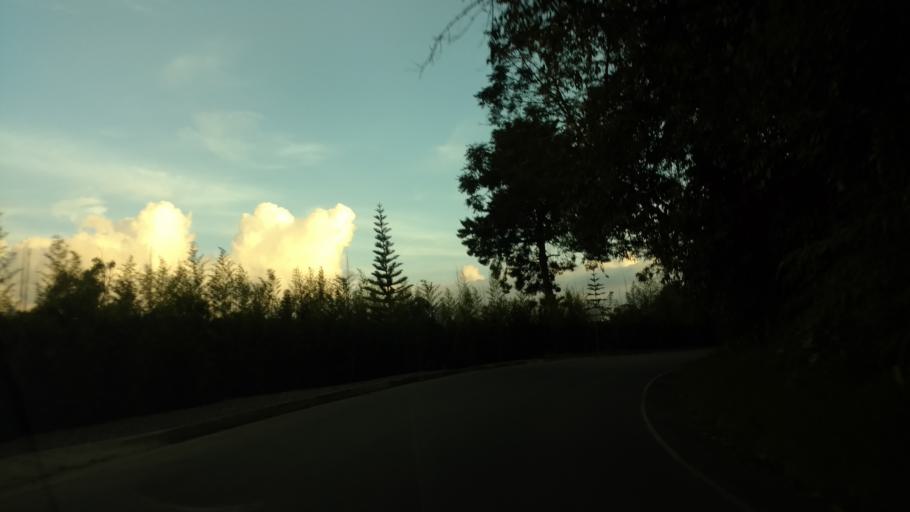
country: CO
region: Caldas
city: Aranzazu
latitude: 5.2896
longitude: -75.4886
